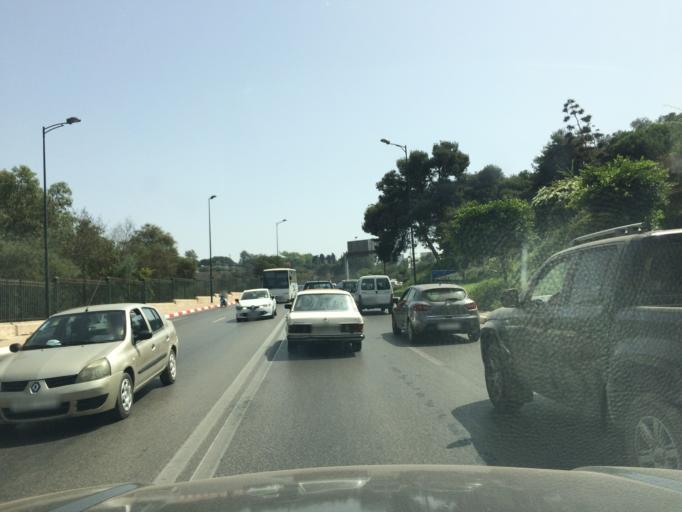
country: MA
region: Rabat-Sale-Zemmour-Zaer
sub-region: Rabat
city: Rabat
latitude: 34.0190
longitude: -6.8199
